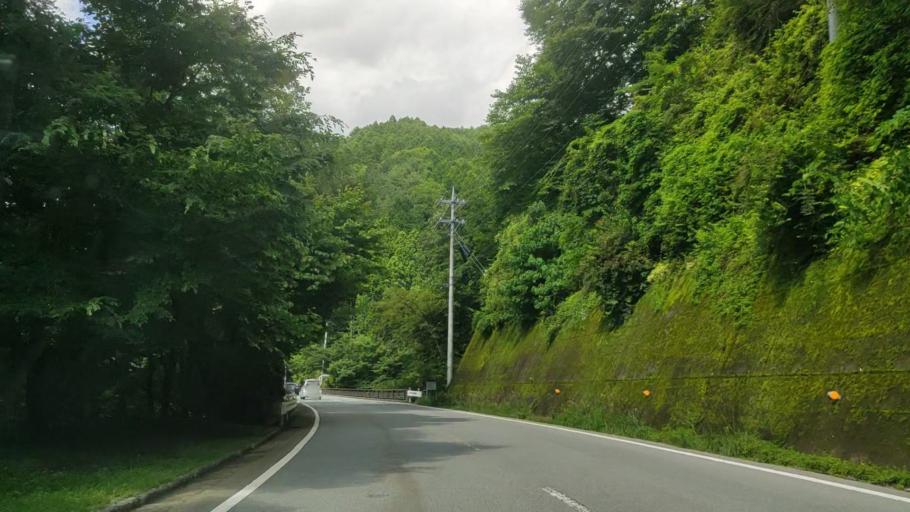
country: JP
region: Yamanashi
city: Enzan
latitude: 35.8373
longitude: 138.7667
